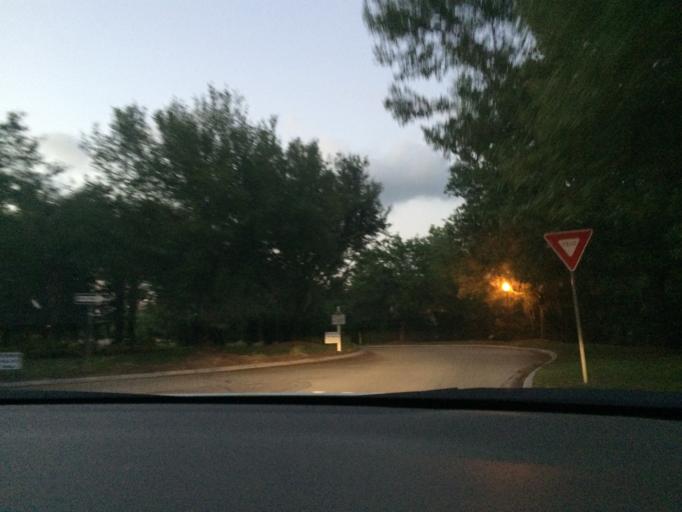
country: US
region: Florida
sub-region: Manatee County
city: Ellenton
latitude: 27.4933
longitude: -82.4113
